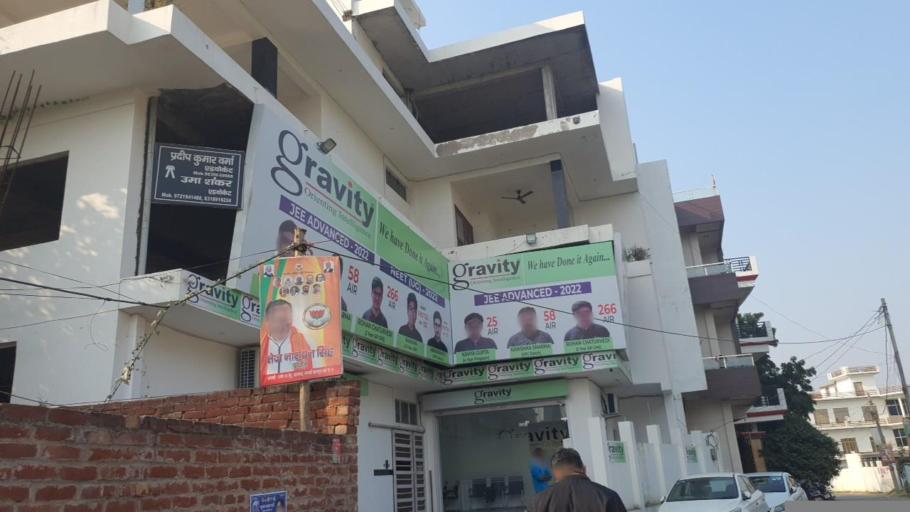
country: IN
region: Uttar Pradesh
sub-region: Lucknow District
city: Lucknow
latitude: 26.7949
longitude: 81.0098
